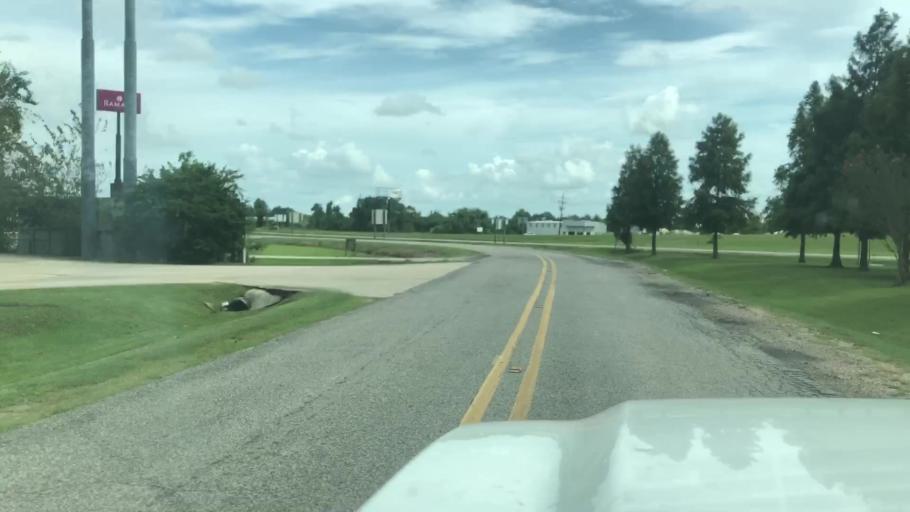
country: US
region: Louisiana
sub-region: Iberia Parish
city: New Iberia
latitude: 29.9849
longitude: -91.8571
